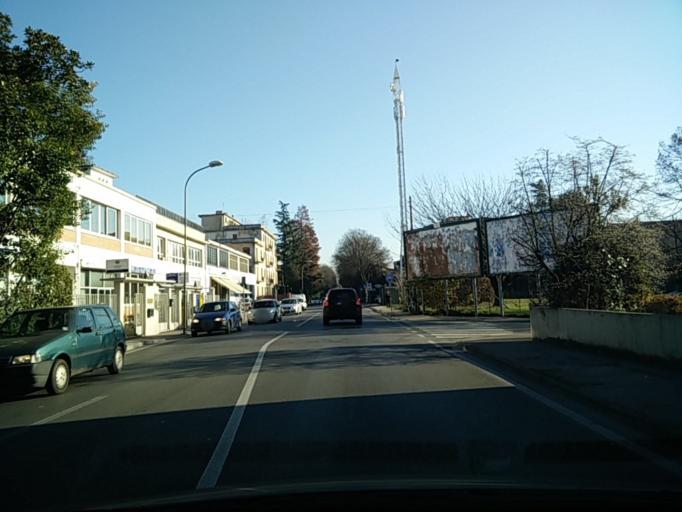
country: IT
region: Veneto
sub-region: Provincia di Treviso
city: Treviso
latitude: 45.6768
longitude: 12.2537
